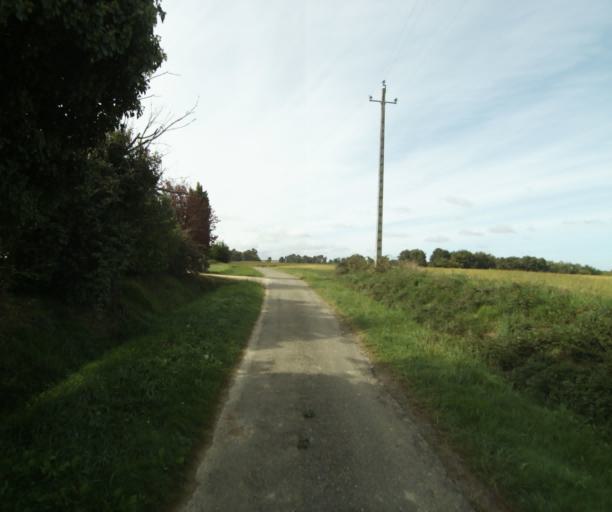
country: FR
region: Midi-Pyrenees
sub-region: Departement du Gers
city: Eauze
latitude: 43.8634
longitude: 0.1478
